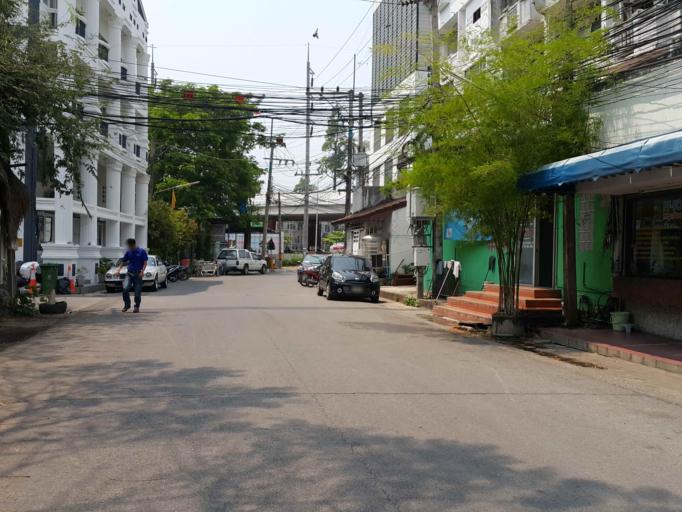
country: TH
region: Chiang Mai
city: Chiang Mai
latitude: 18.7576
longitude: 99.0084
